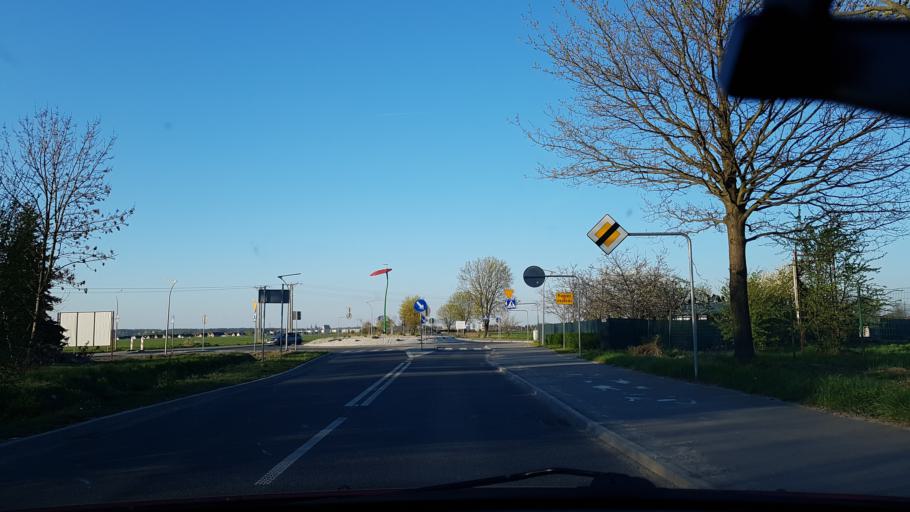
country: PL
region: Opole Voivodeship
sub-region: Powiat nyski
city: Nysa
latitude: 50.4389
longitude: 17.3099
